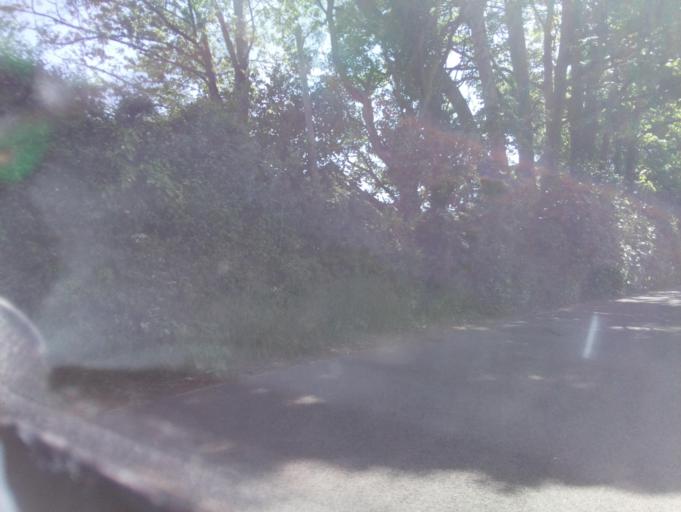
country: GB
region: Wales
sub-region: Monmouthshire
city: Caldicot
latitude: 51.6403
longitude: -2.7546
